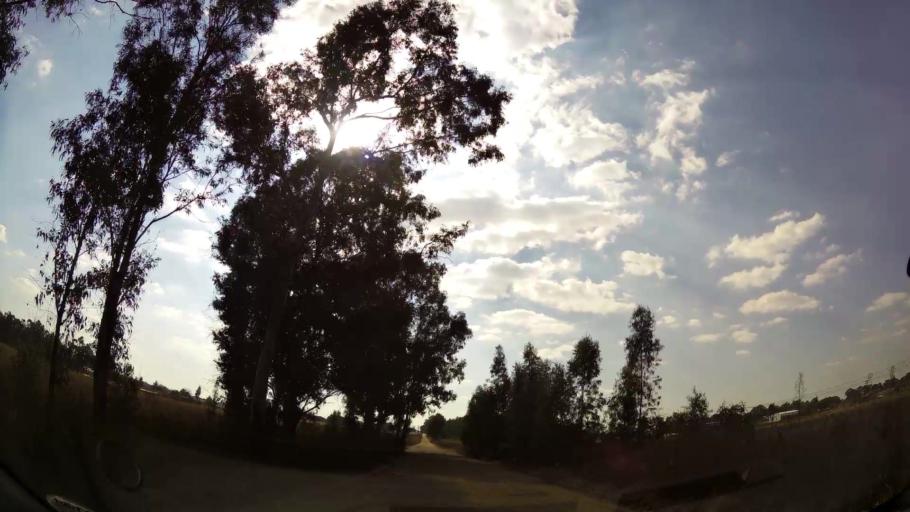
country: ZA
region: Gauteng
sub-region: Ekurhuleni Metropolitan Municipality
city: Benoni
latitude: -26.0854
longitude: 28.3681
